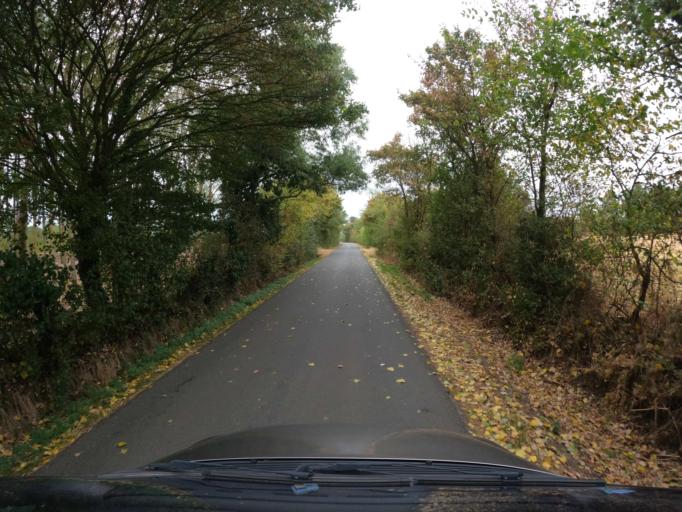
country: FR
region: Pays de la Loire
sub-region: Departement de Maine-et-Loire
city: Saint-Christophe-du-Bois
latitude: 47.0430
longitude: -0.9794
